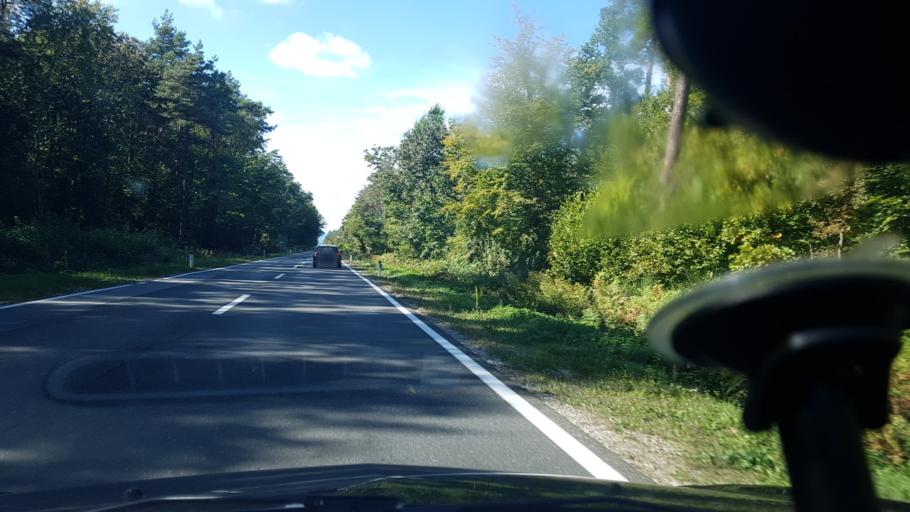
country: SI
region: Kidricevo
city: Kidricevo
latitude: 46.4108
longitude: 15.7763
